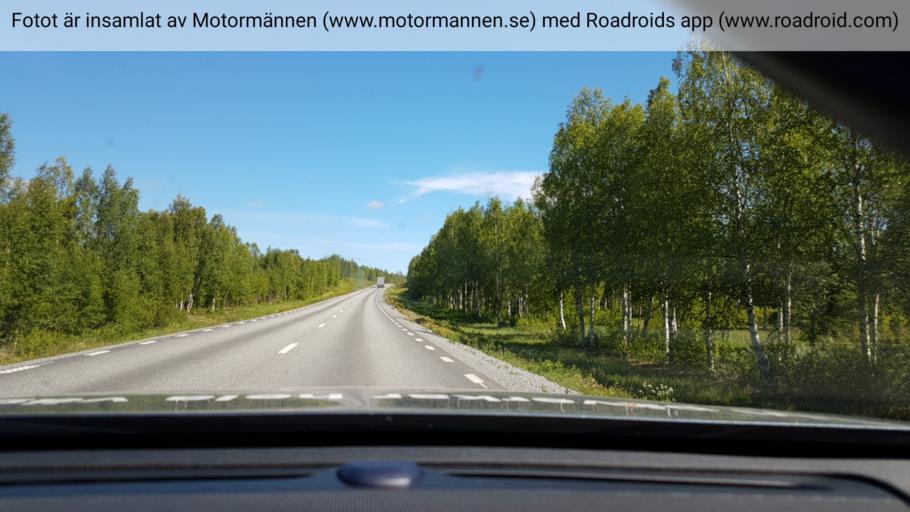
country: SE
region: Vaesterbotten
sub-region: Vilhelmina Kommun
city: Vilhelmina
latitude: 64.6592
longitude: 16.6580
